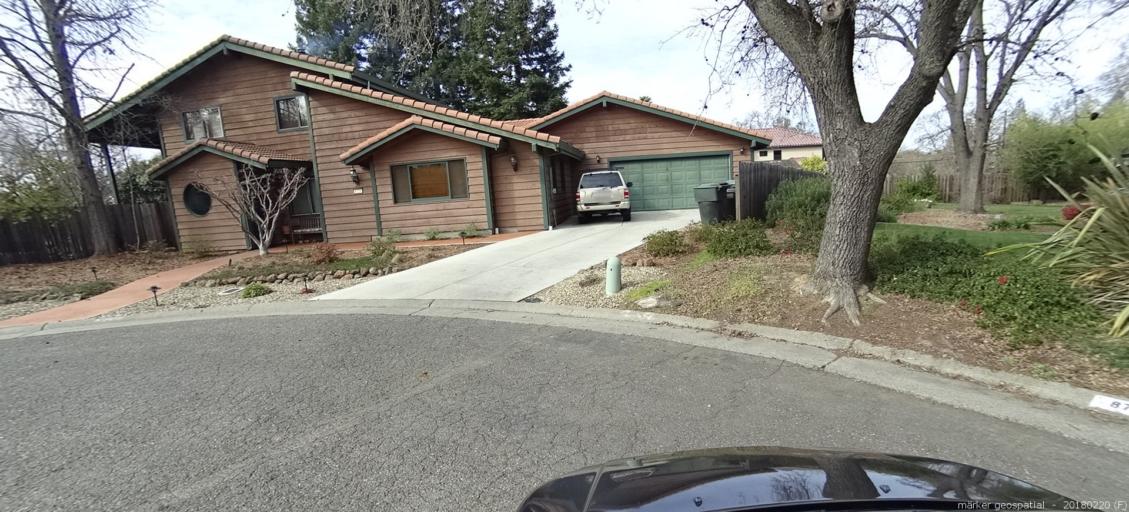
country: US
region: California
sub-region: Sacramento County
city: Orangevale
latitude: 38.6889
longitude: -121.2336
